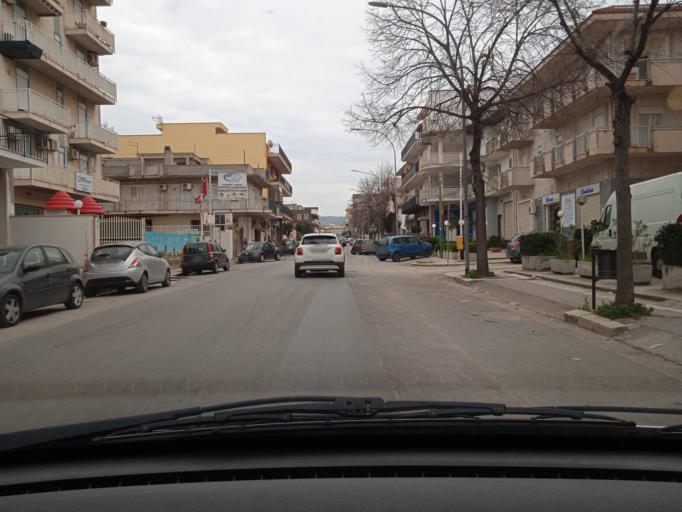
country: IT
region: Sicily
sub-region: Palermo
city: Villabate
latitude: 38.0784
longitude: 13.4454
